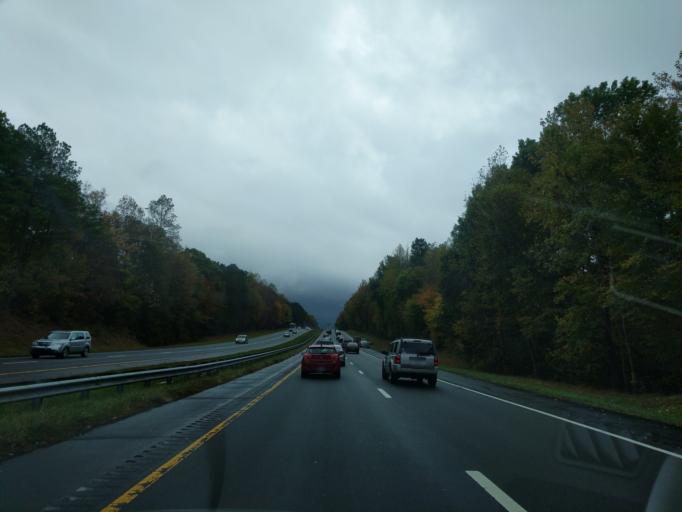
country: US
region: North Carolina
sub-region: Orange County
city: Hillsborough
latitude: 36.0540
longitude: -79.0676
